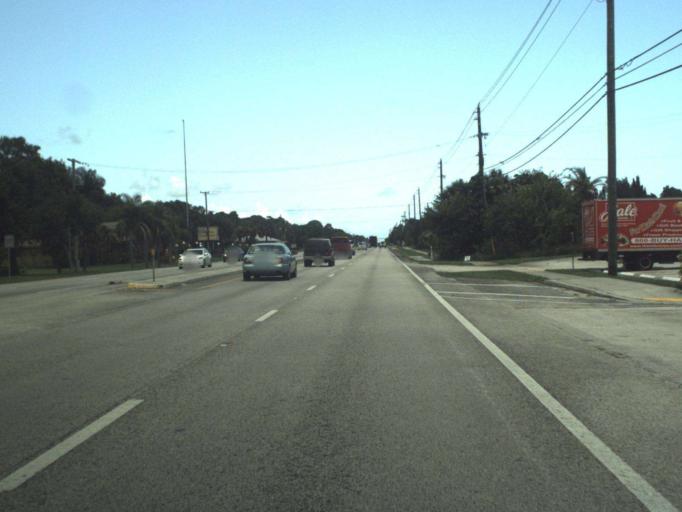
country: US
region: Florida
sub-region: Indian River County
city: Wabasso Beach
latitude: 27.7616
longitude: -80.4408
